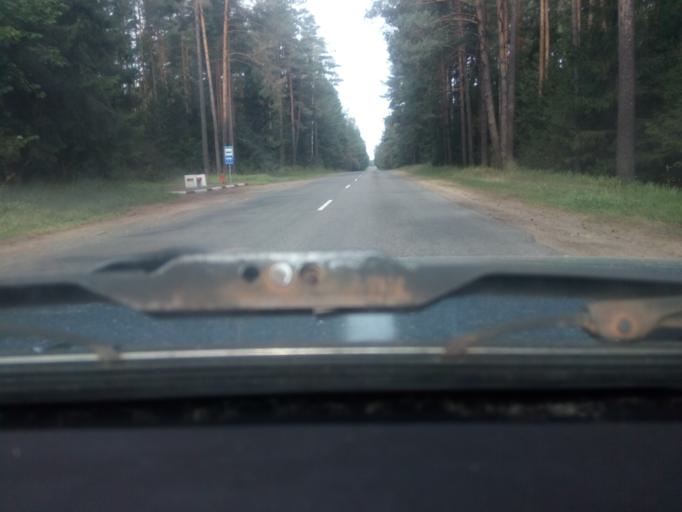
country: BY
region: Vitebsk
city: Vyerkhnyadzvinsk
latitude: 55.7936
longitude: 27.9668
